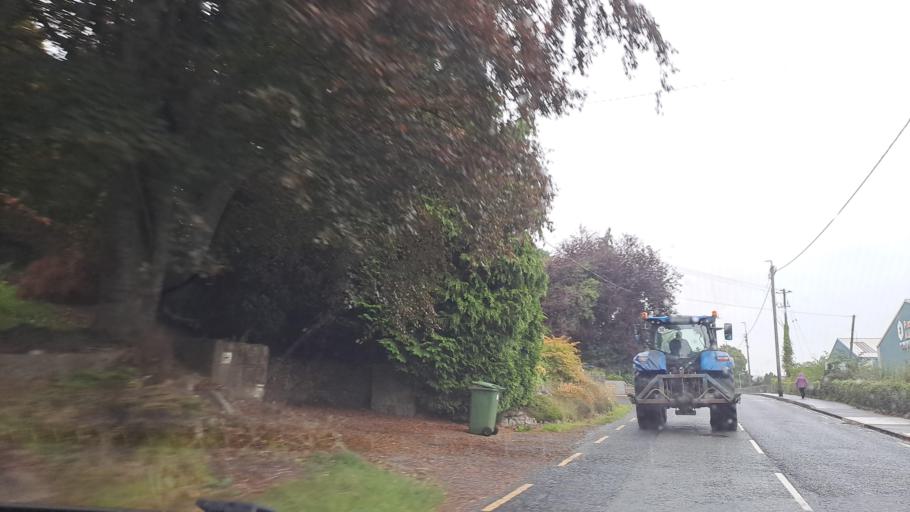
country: IE
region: Ulster
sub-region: County Monaghan
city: Carrickmacross
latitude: 53.9747
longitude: -6.7110
